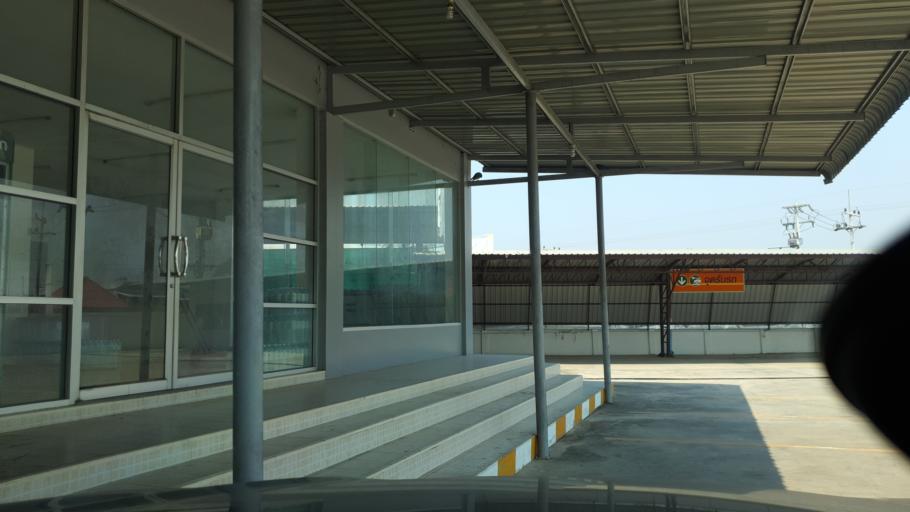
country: TH
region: Nakhon Sawan
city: Nakhon Sawan
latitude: 15.6551
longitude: 100.0746
